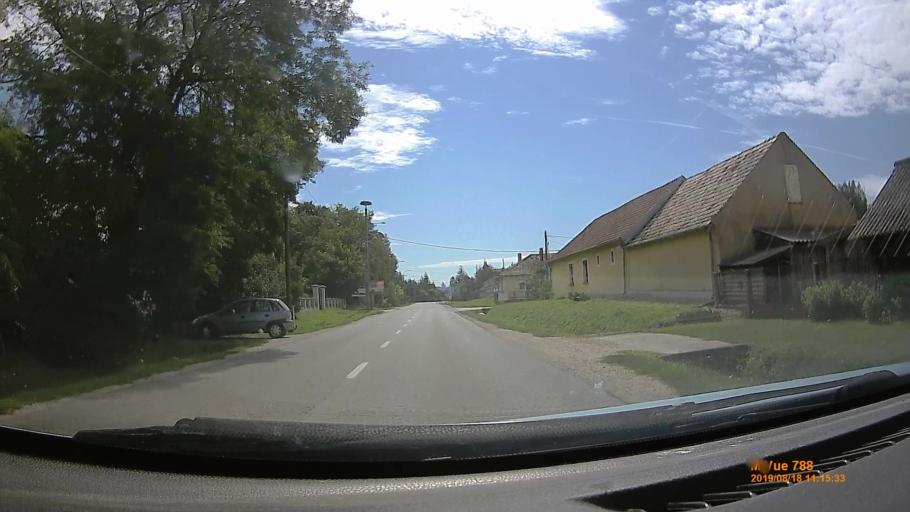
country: HU
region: Fejer
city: Szabadbattyan
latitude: 47.0843
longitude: 18.4051
